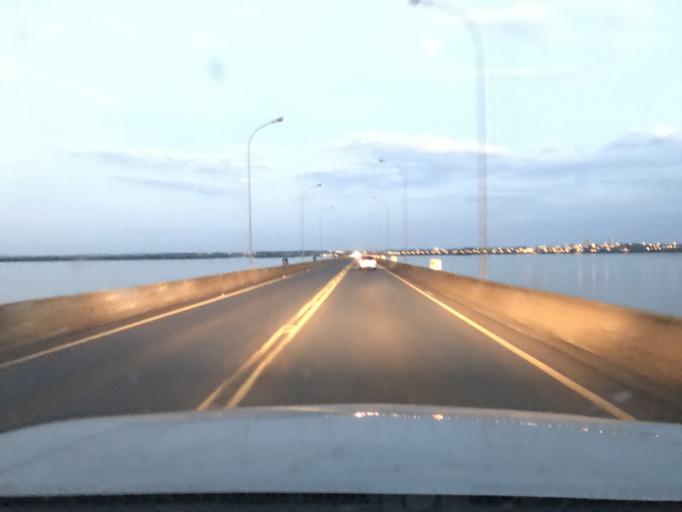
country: PY
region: Canindeyu
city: Salto del Guaira
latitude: -24.0470
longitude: -54.2696
